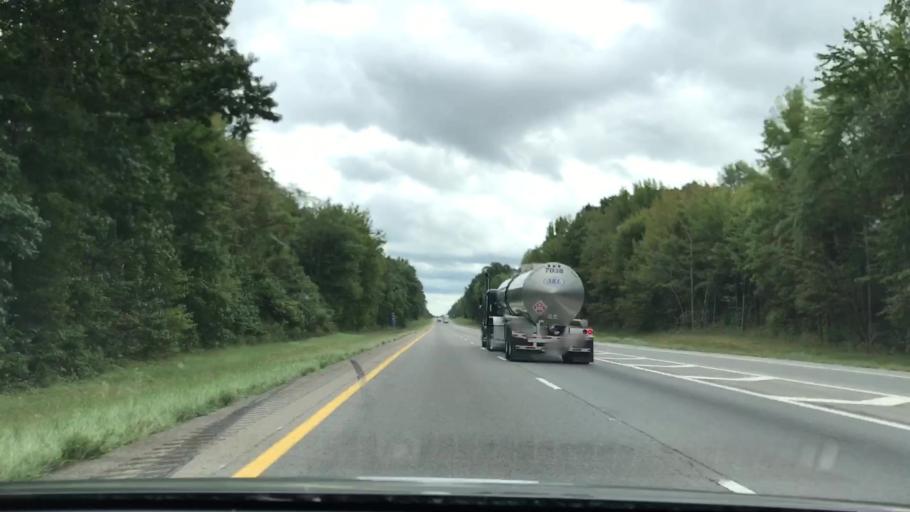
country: US
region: Tennessee
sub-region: Cheatham County
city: Pleasant View
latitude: 36.4471
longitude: -87.0953
